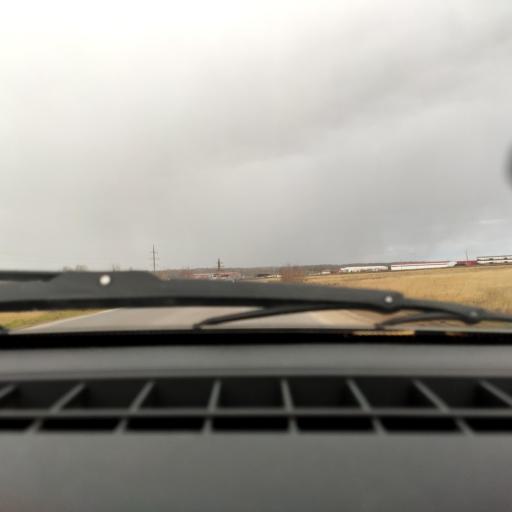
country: RU
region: Bashkortostan
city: Iglino
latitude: 54.7617
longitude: 56.2619
